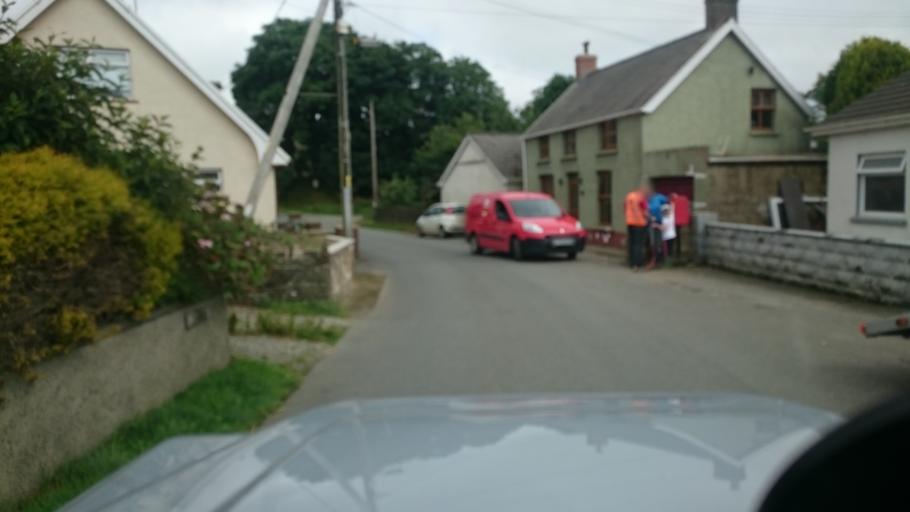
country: GB
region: Wales
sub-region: Pembrokeshire
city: Ambleston
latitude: 51.9227
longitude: -4.9412
